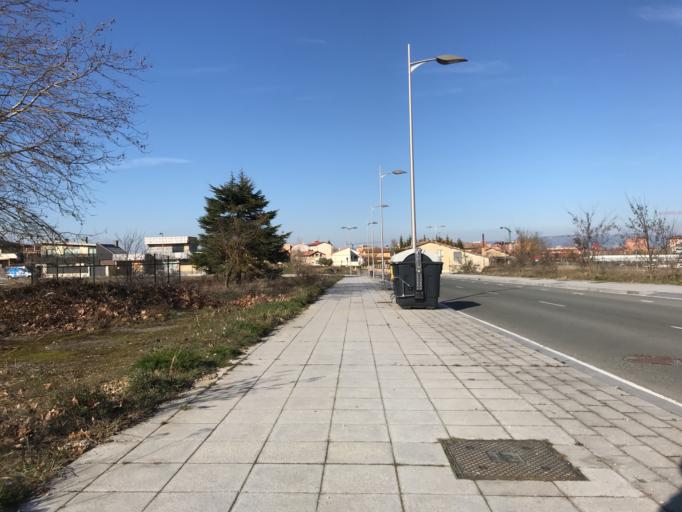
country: ES
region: Basque Country
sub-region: Provincia de Alava
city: Gasteiz / Vitoria
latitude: 42.8282
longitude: -2.6740
